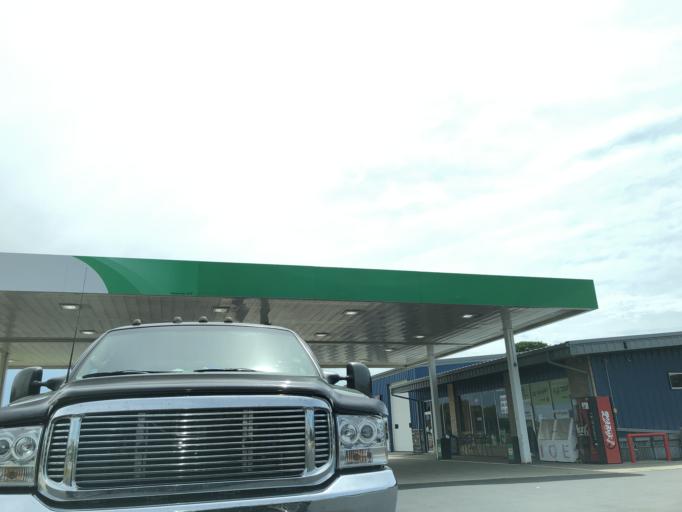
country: US
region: Minnesota
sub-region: Stearns County
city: Melrose
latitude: 45.6701
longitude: -94.8120
